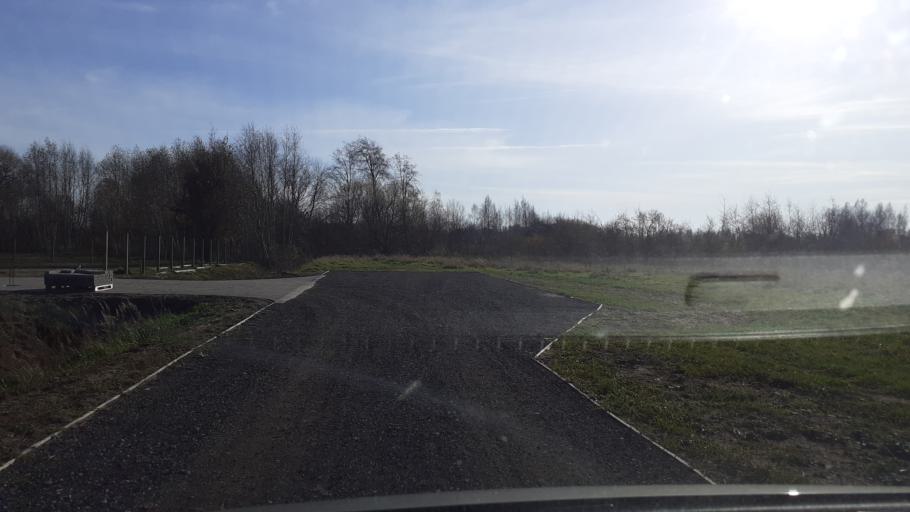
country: LV
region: Kuldigas Rajons
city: Kuldiga
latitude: 56.9571
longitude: 21.9974
